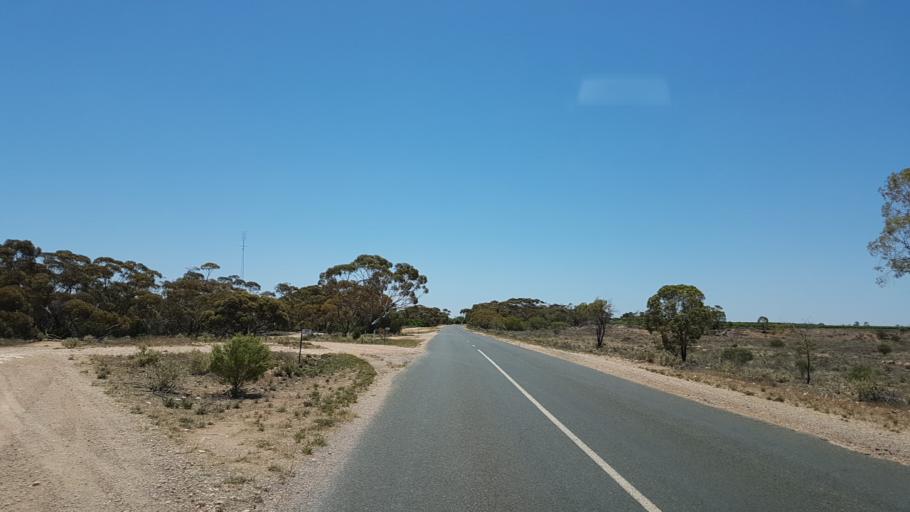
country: AU
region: South Australia
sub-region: Loxton Waikerie
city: Waikerie
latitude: -34.1811
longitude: 140.0241
